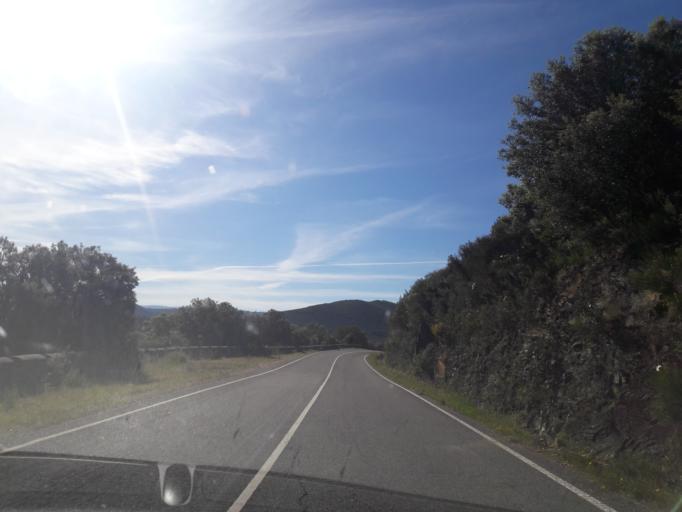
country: ES
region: Castille and Leon
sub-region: Provincia de Salamanca
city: Sotoserrano
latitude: 40.4220
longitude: -6.0366
